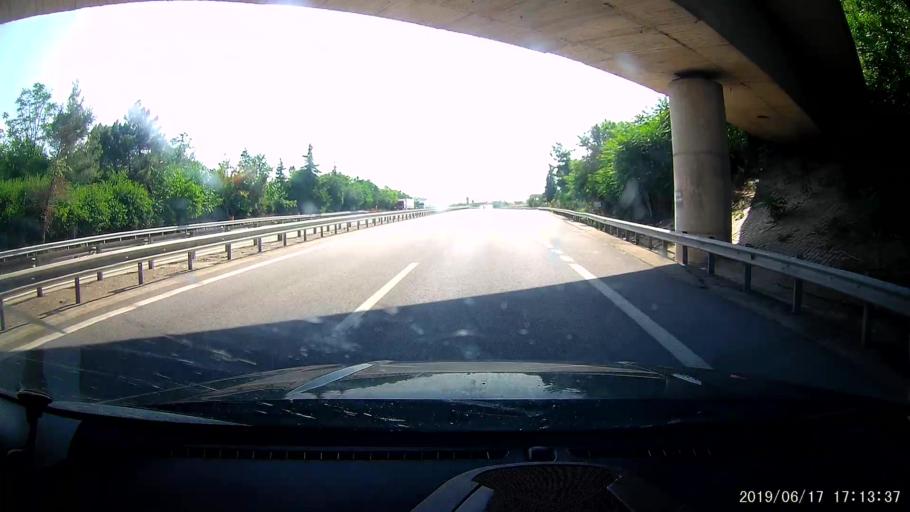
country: TR
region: Edirne
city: Edirne
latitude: 41.7006
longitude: 26.5366
